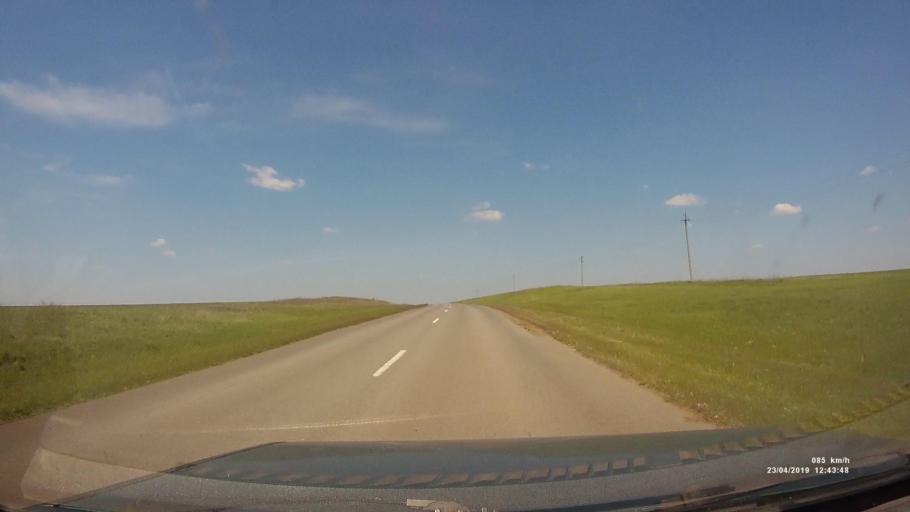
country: RU
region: Kalmykiya
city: Yashalta
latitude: 46.4687
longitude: 42.6501
